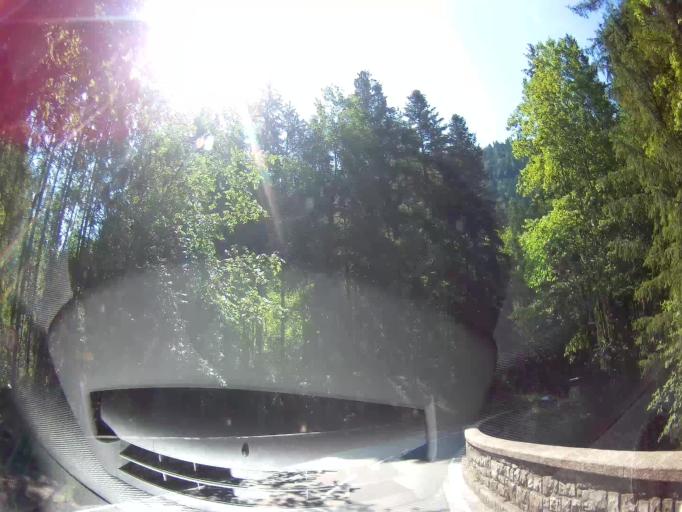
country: AT
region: Salzburg
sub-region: Politischer Bezirk Hallein
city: Hallein
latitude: 47.6419
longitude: 13.0620
